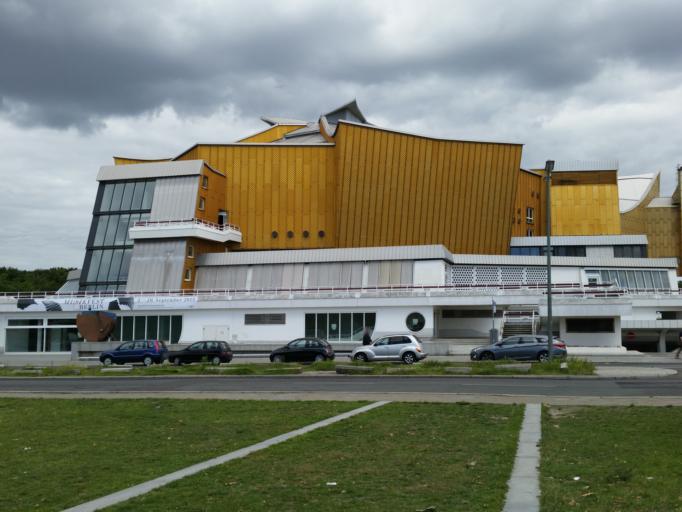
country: DE
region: Berlin
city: Tiergarten Bezirk
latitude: 52.5086
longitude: 13.3687
